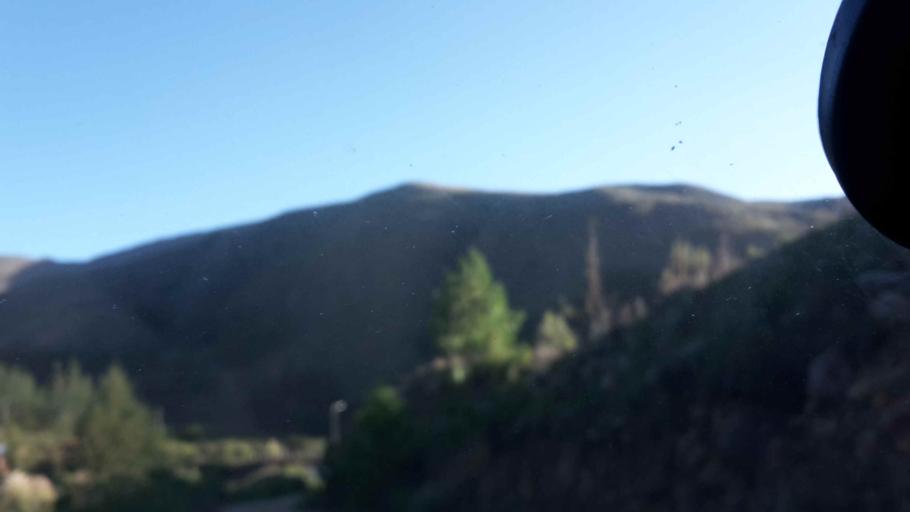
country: BO
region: Cochabamba
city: Arani
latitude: -17.7965
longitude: -65.5991
